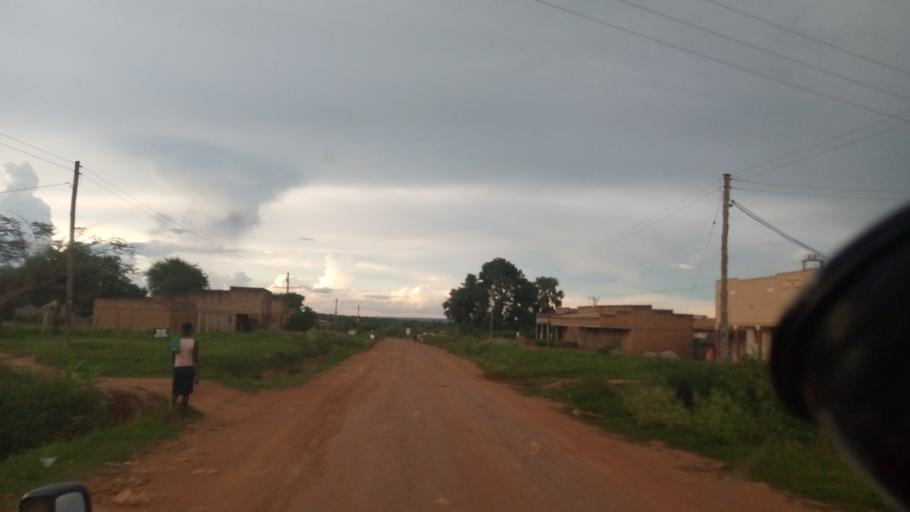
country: UG
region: Northern Region
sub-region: Kole District
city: Kole
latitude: 2.4894
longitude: 32.9349
